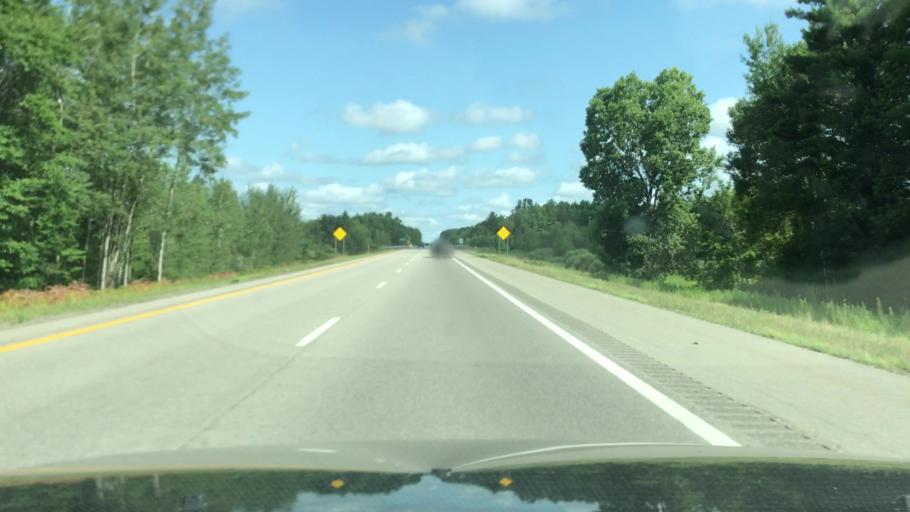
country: US
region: Michigan
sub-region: Mecosta County
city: Big Rapids
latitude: 43.5523
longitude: -85.4872
